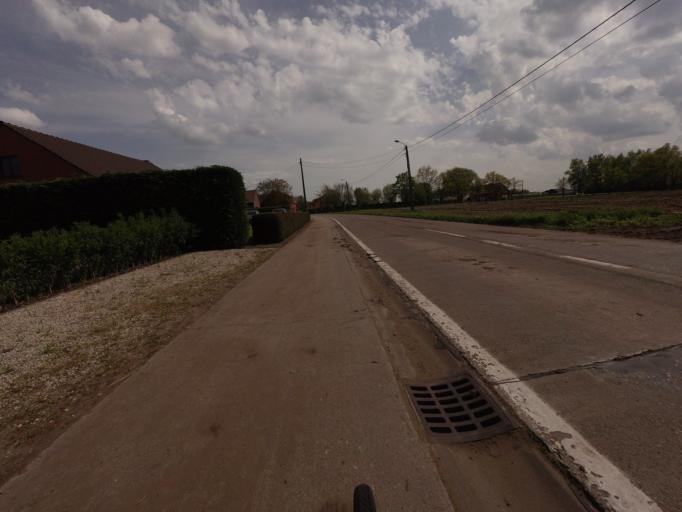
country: BE
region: Flanders
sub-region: Provincie Antwerpen
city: Putte
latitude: 51.0722
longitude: 4.6033
